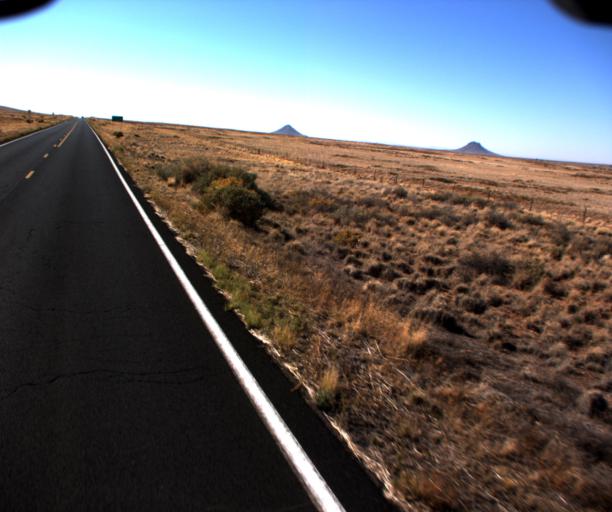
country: US
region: Arizona
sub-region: Navajo County
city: Dilkon
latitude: 35.4507
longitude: -110.4235
